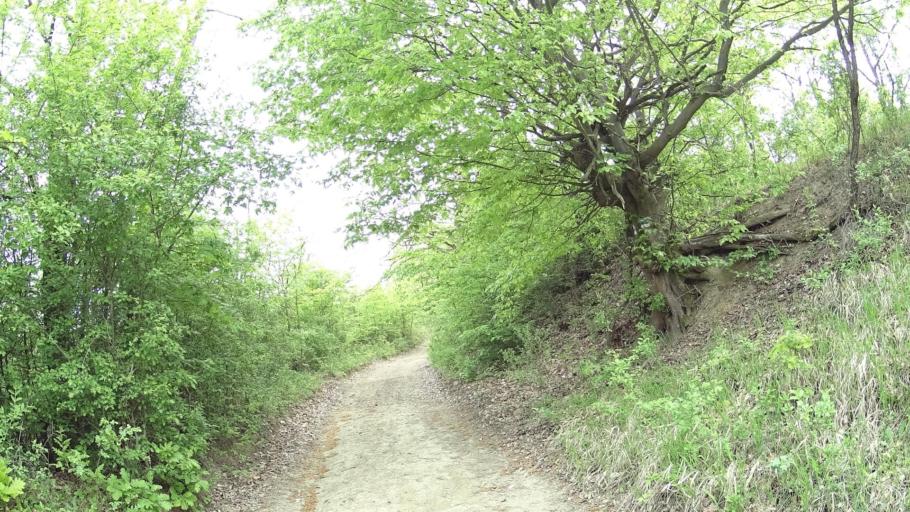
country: HU
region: Nograd
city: Romhany
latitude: 47.9301
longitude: 19.2971
